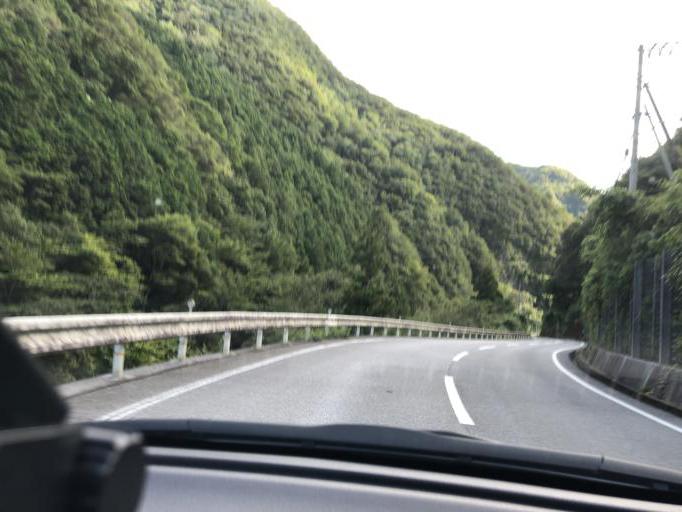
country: JP
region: Kochi
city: Kochi-shi
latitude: 33.6327
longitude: 133.5192
